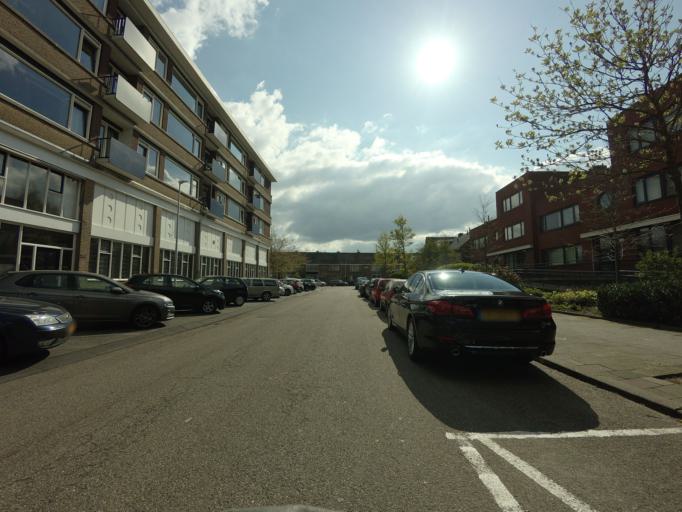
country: NL
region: Utrecht
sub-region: Gemeente Utrecht
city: Lunetten
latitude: 52.0716
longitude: 5.1252
